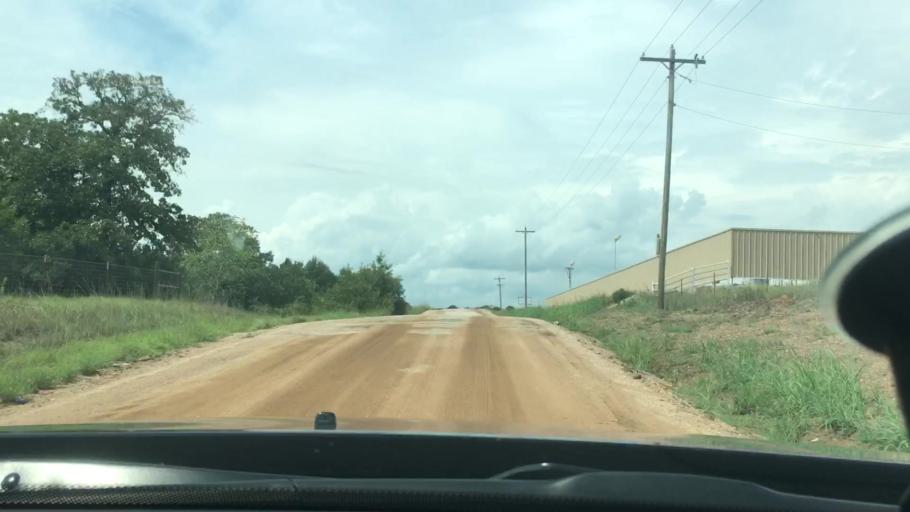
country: US
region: Oklahoma
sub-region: Carter County
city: Dickson
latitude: 34.2454
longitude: -96.9188
